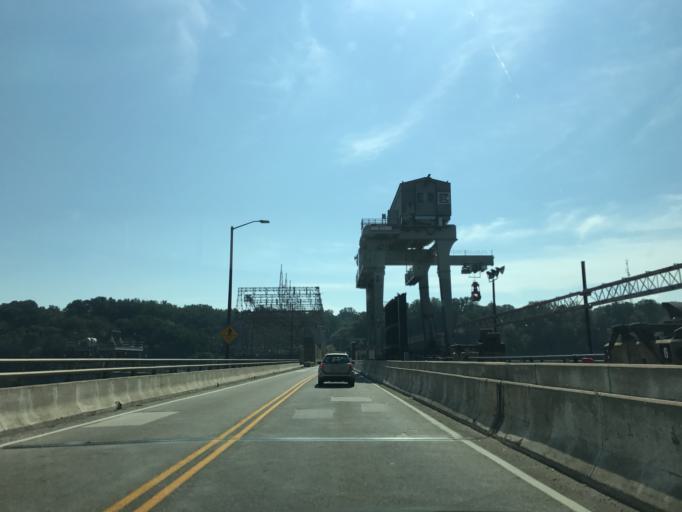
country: US
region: Maryland
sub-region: Cecil County
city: Rising Sun
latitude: 39.6600
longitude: -76.1739
